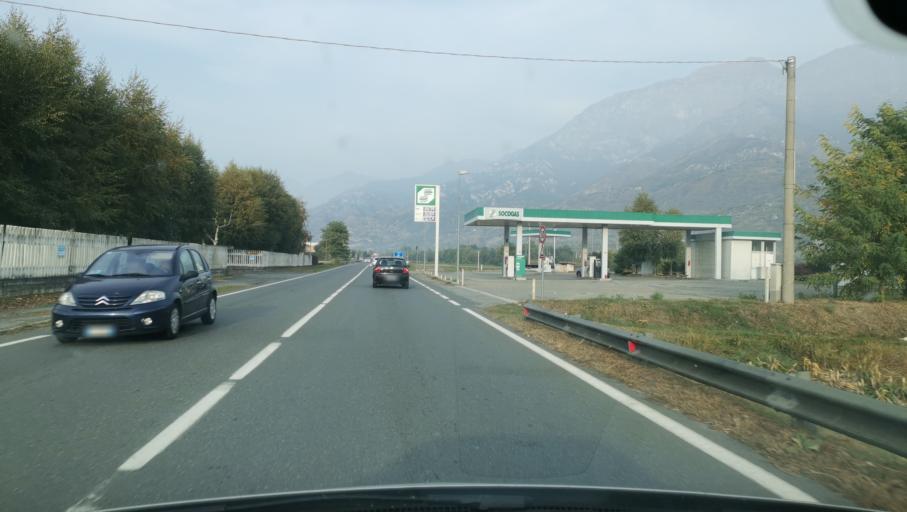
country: IT
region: Piedmont
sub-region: Provincia di Torino
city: Bruzolo
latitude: 45.1312
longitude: 7.1980
